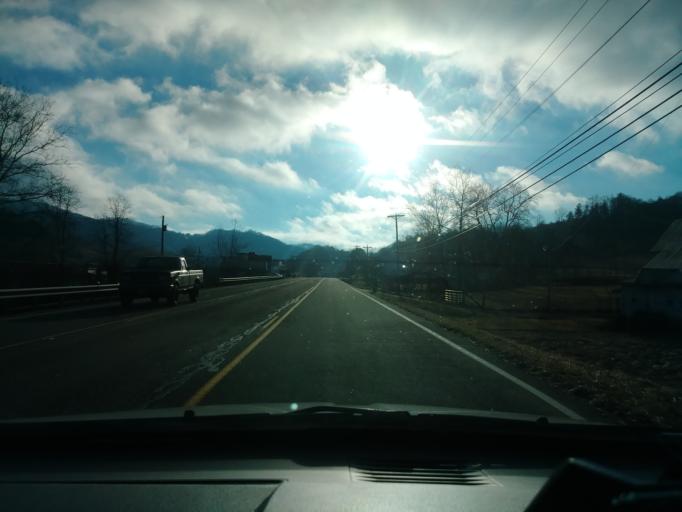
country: US
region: Tennessee
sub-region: Carter County
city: Roan Mountain
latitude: 36.1907
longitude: -82.0470
